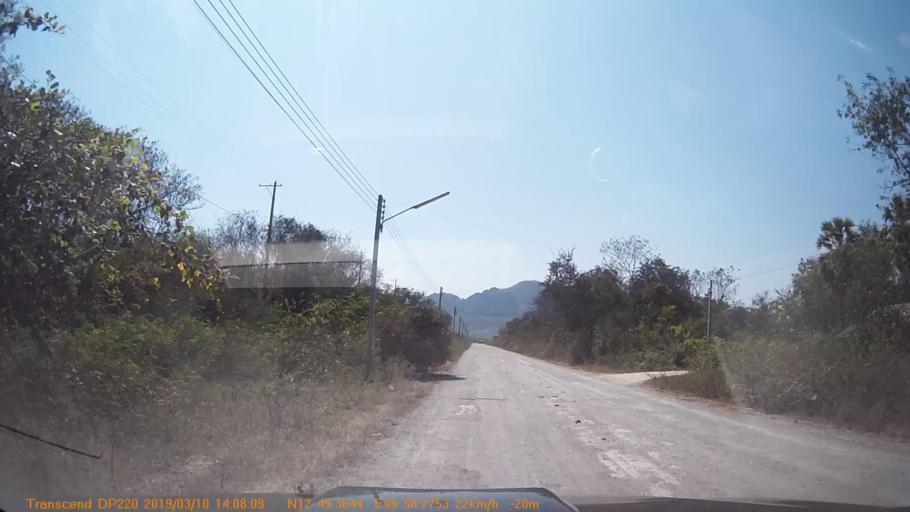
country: TH
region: Phetchaburi
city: Cha-am
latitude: 12.8227
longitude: 99.9795
